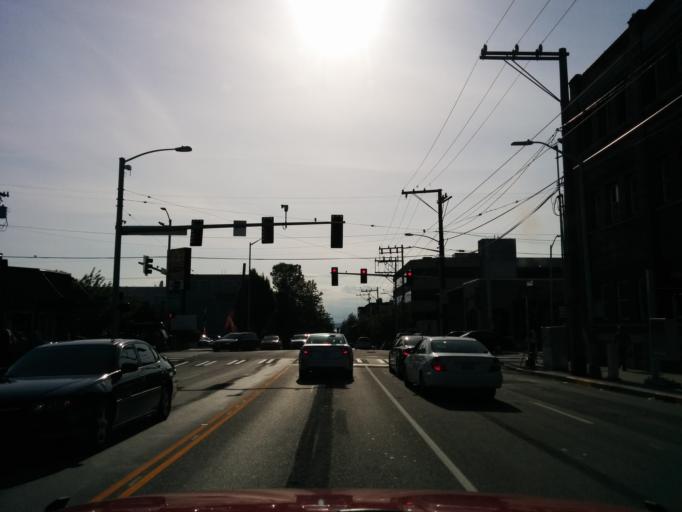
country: US
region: Washington
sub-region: King County
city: Seattle
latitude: 47.6246
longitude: -122.3562
